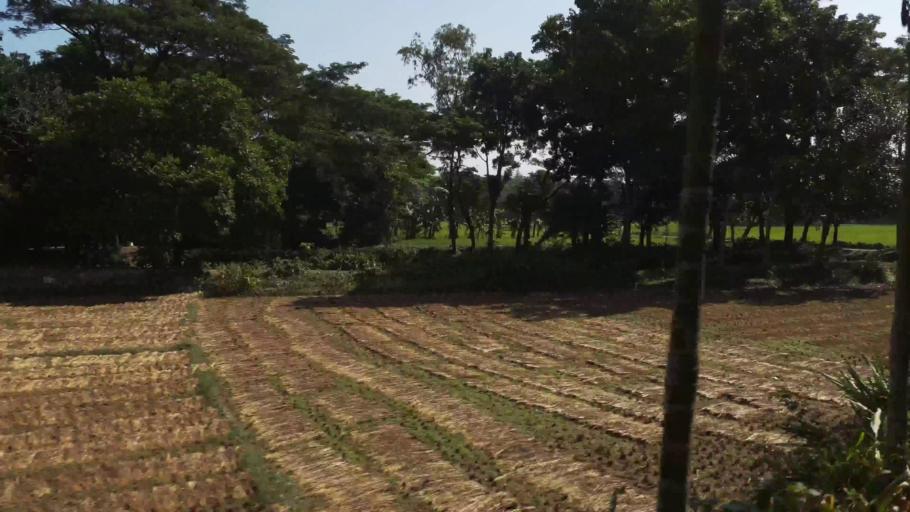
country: BD
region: Dhaka
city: Gafargaon
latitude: 24.5366
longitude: 90.5086
